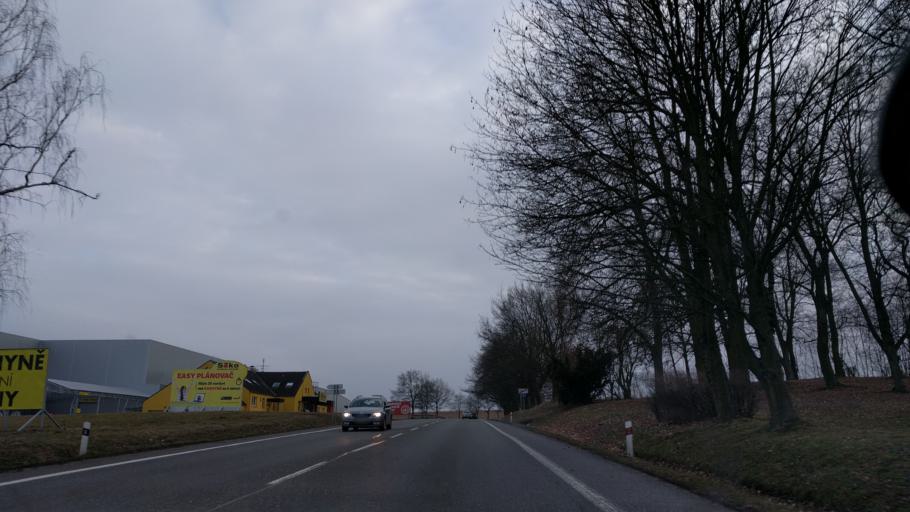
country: CZ
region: Jihocesky
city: Cimelice
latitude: 49.4620
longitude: 14.0682
